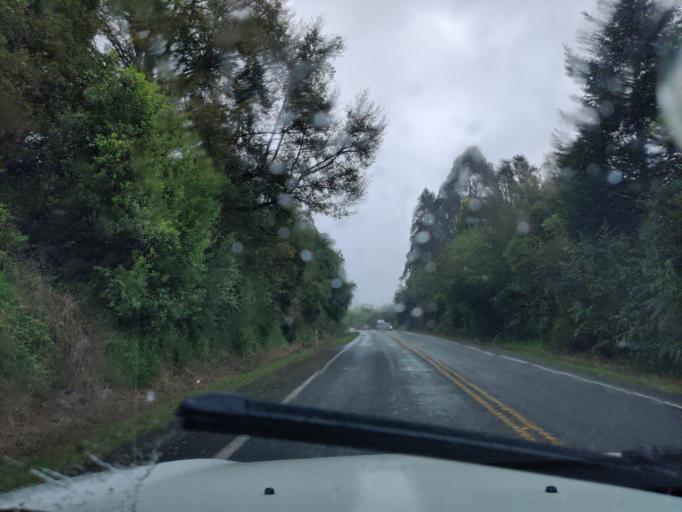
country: NZ
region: Bay of Plenty
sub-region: Rotorua District
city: Rotorua
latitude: -38.0797
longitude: 176.1852
